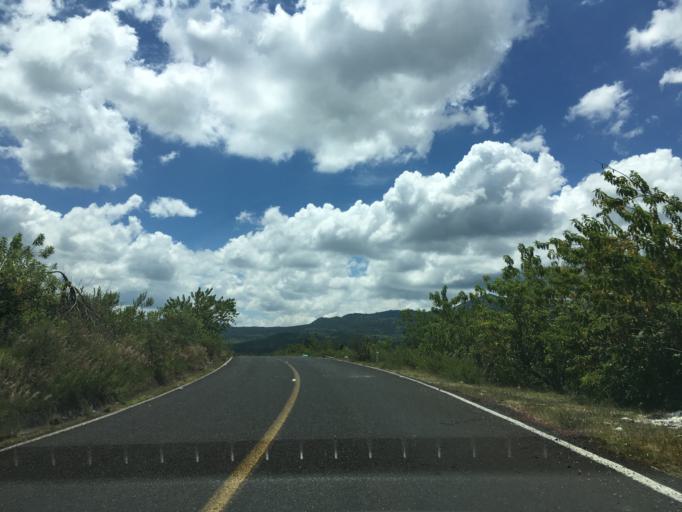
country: MX
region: Mexico
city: Huaniqueo de Morales
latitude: 19.7988
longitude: -101.4575
